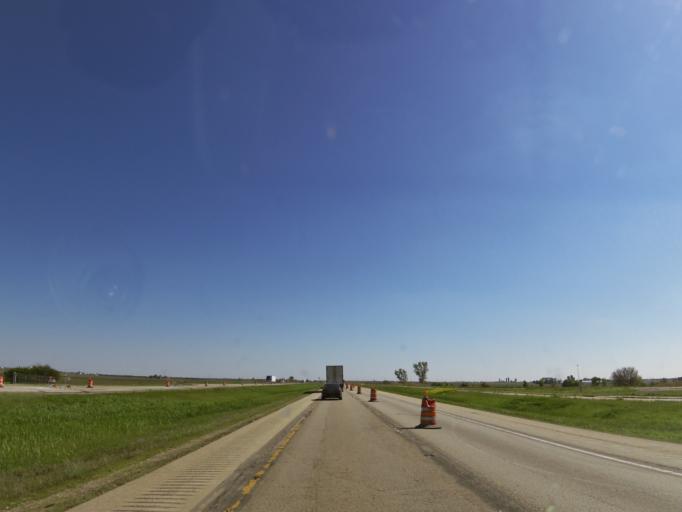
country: US
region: Illinois
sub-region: Ogle County
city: Hillcrest
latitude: 41.9686
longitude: -89.0224
